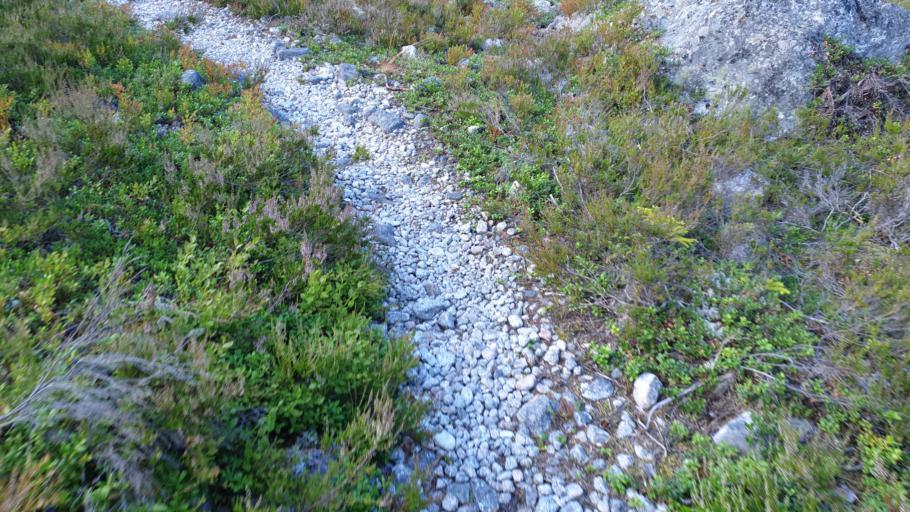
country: SE
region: Gaevleborg
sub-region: Soderhamns Kommun
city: Marielund
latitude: 61.4239
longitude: 17.1535
